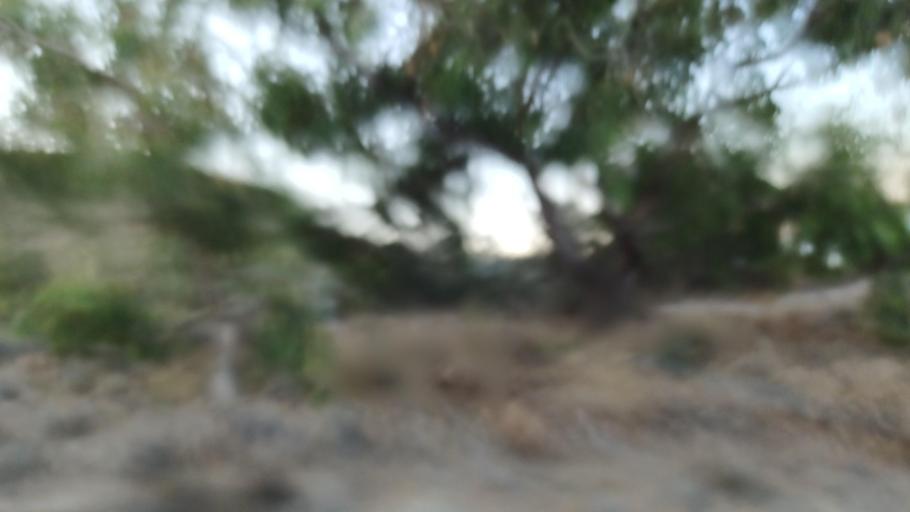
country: CY
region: Larnaka
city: Pyla
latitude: 34.9835
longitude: 33.7045
